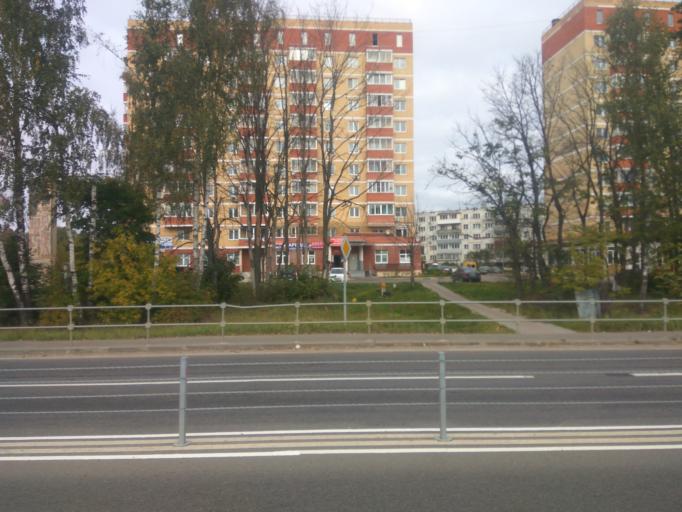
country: RU
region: Moskovskaya
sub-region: Shchelkovskiy Rayon
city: Grebnevo
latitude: 56.0063
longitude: 38.1402
